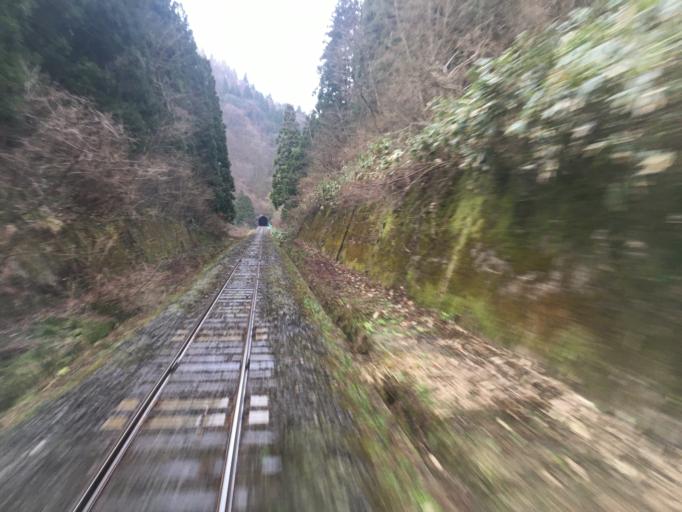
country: JP
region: Akita
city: Kakunodatemachi
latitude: 39.7113
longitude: 140.5532
